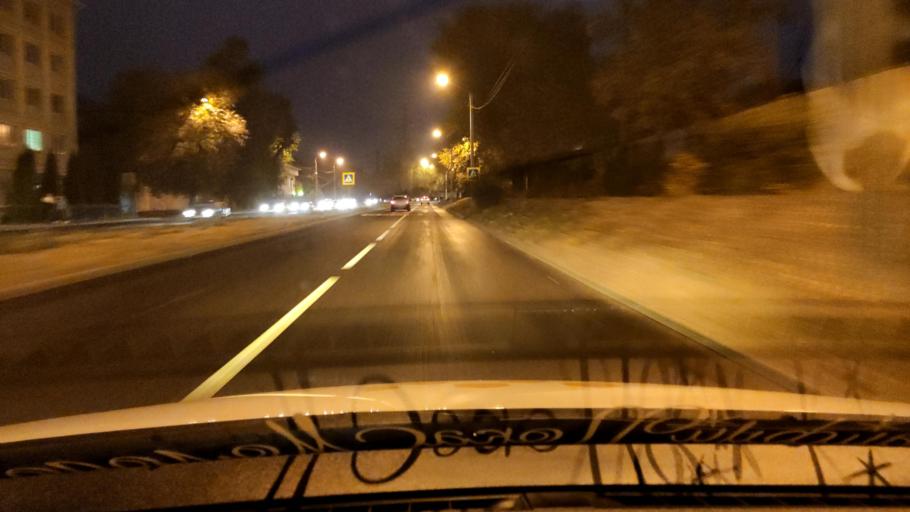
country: RU
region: Voronezj
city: Voronezh
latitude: 51.6898
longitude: 39.1618
